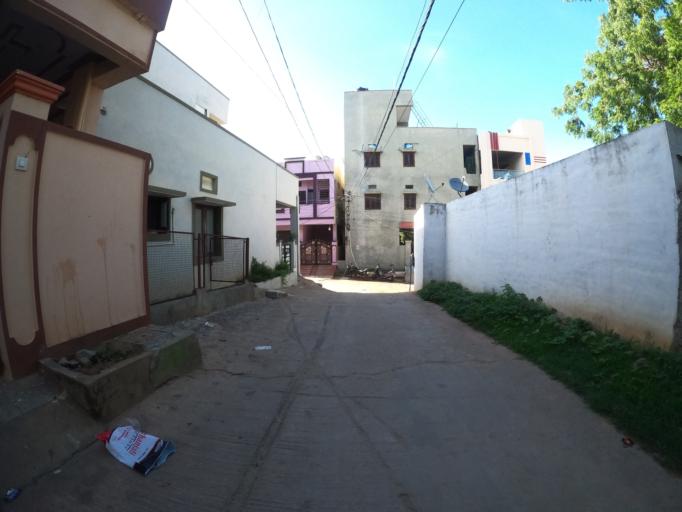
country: IN
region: Telangana
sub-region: Hyderabad
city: Hyderabad
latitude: 17.3581
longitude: 78.3794
